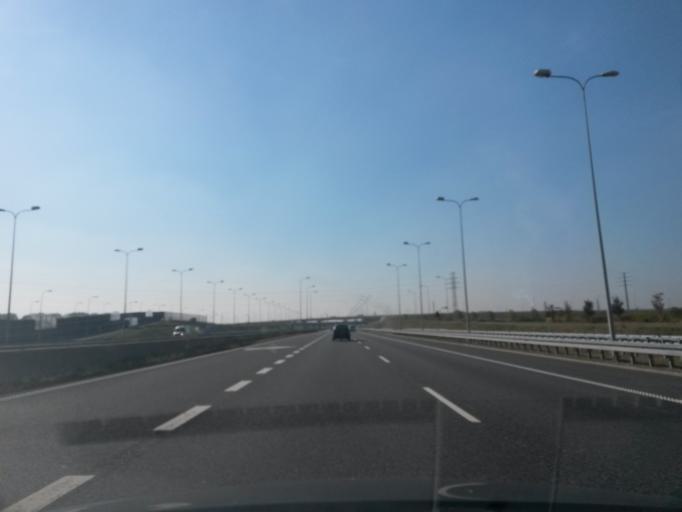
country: PL
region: Silesian Voivodeship
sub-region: Powiat gliwicki
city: Przyszowice
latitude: 50.2636
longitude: 18.7309
